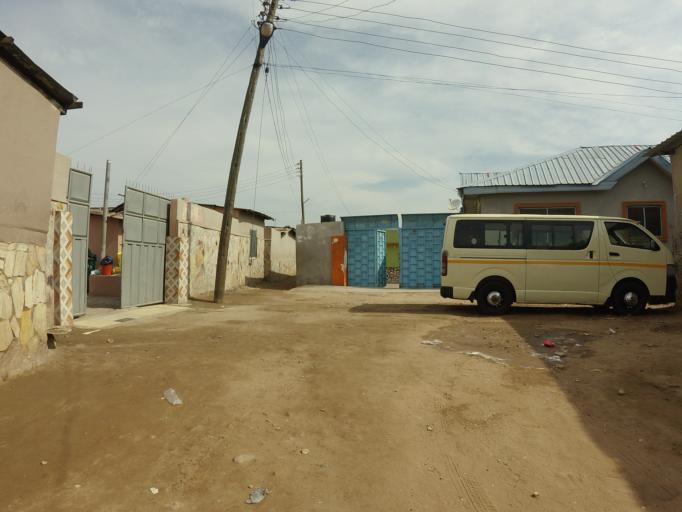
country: GH
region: Greater Accra
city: Dome
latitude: 5.6261
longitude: -0.2299
